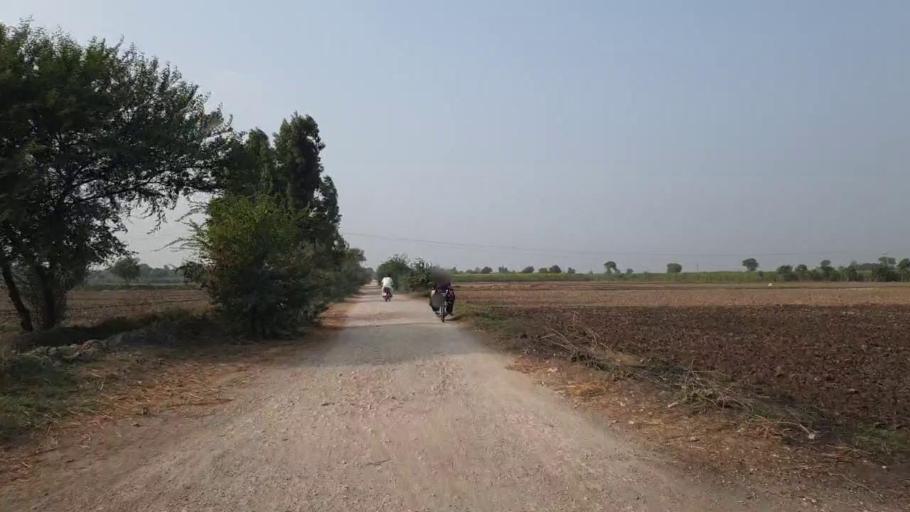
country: PK
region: Sindh
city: Tando Muhammad Khan
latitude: 25.0823
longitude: 68.5869
